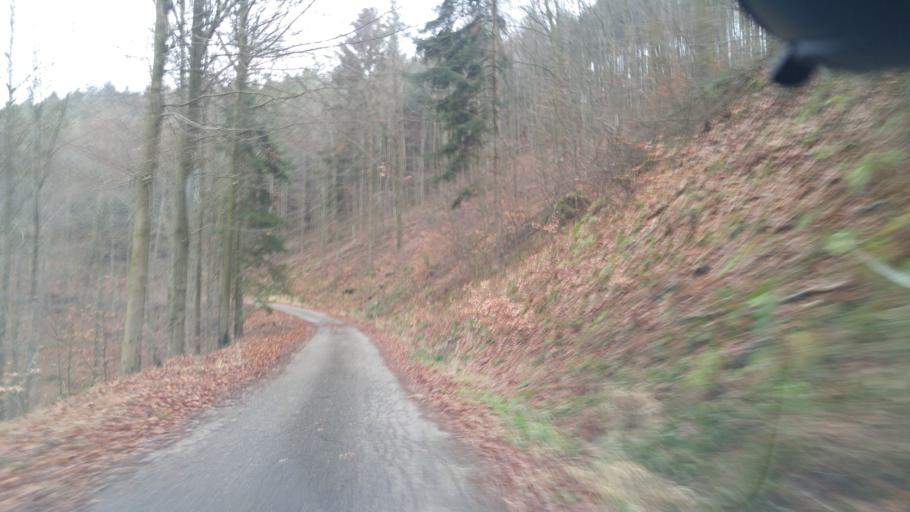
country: DE
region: Rheinland-Pfalz
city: Vorderweidenthal
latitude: 49.1016
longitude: 7.8918
